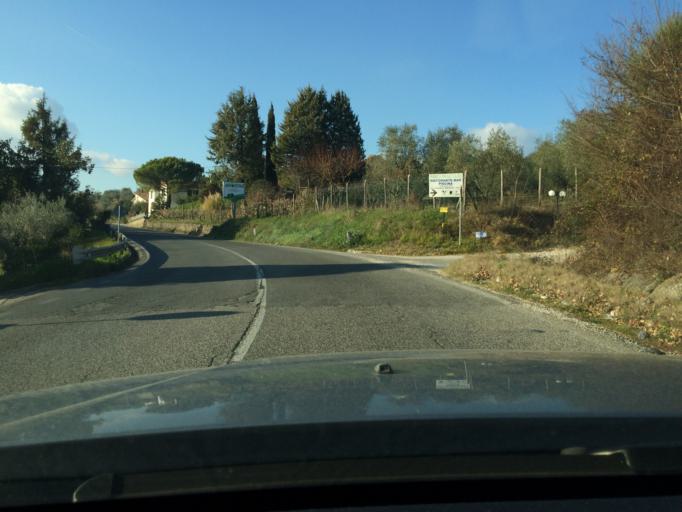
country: IT
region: Umbria
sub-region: Provincia di Terni
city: Amelia
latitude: 42.5578
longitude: 12.4394
